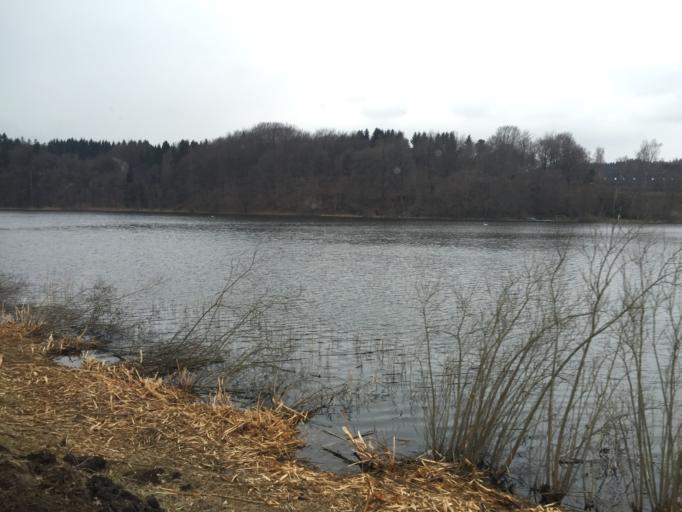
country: DK
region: Central Jutland
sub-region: Silkeborg Kommune
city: Virklund
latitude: 56.0283
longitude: 9.4879
